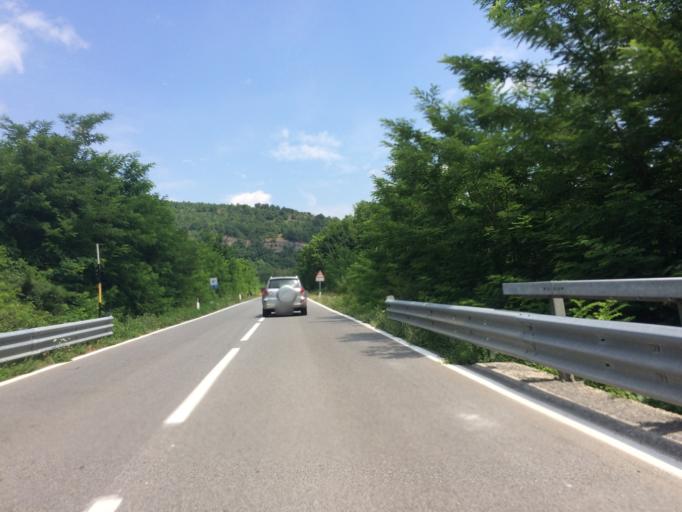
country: IT
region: Piedmont
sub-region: Provincia di Cuneo
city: Bagnasco
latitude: 44.2896
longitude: 8.0342
